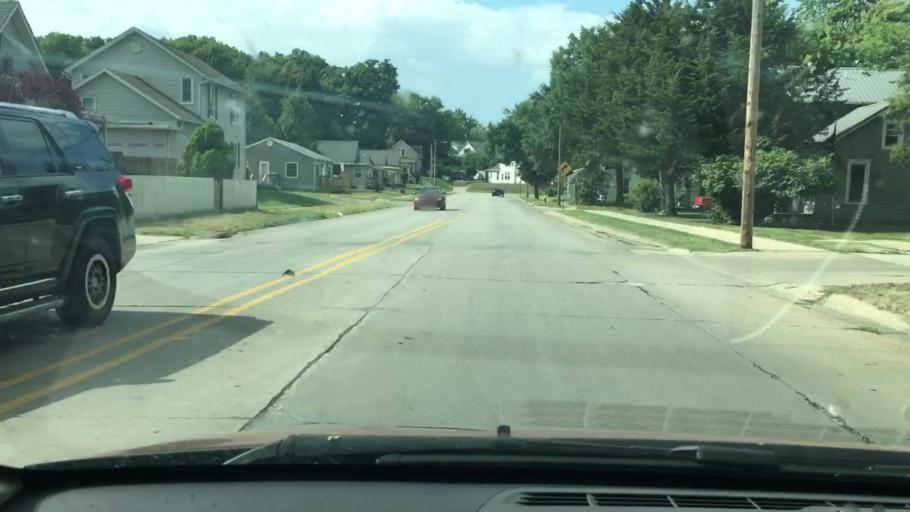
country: US
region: Iowa
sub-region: Muscatine County
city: Muscatine
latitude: 41.4325
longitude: -91.0420
